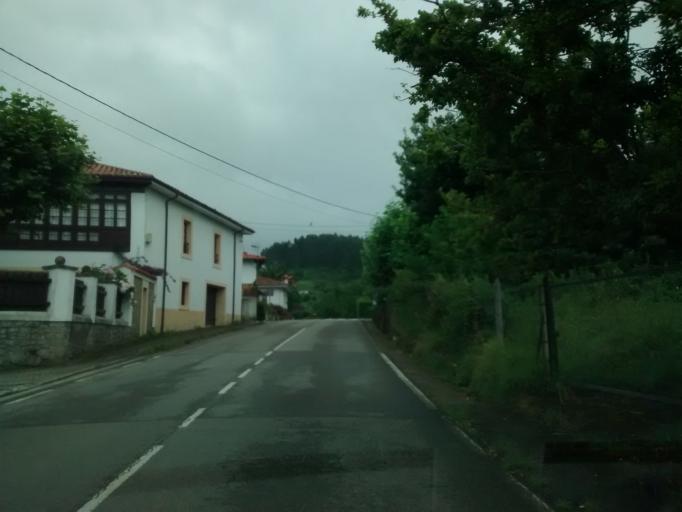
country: ES
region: Asturias
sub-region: Province of Asturias
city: Villaviciosa
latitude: 43.5151
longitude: -5.3671
